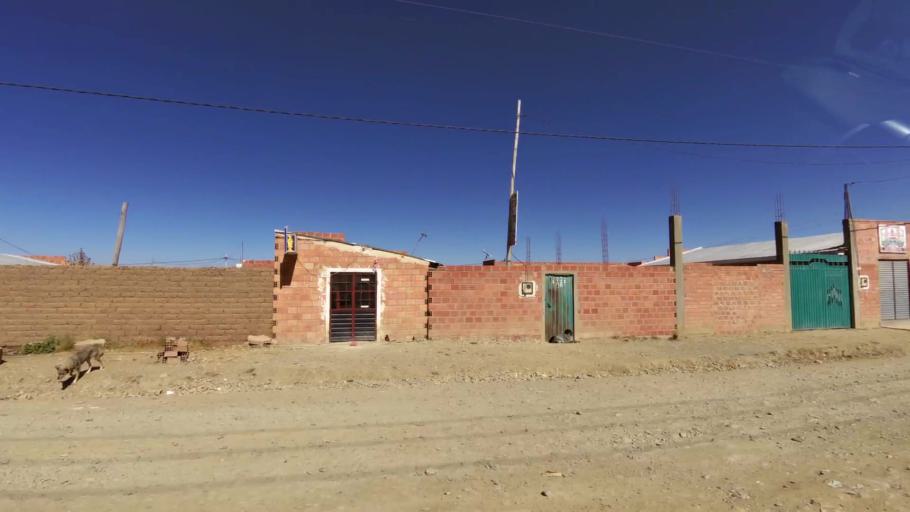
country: BO
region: La Paz
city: La Paz
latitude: -16.6024
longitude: -68.2020
